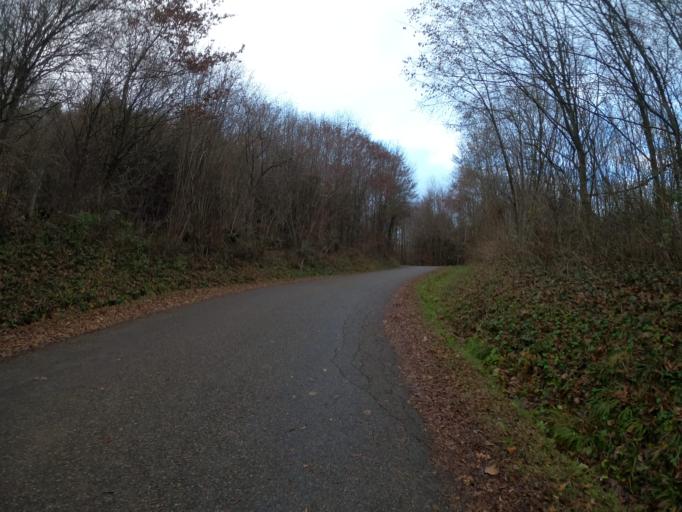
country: DE
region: Baden-Wuerttemberg
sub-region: Regierungsbezirk Stuttgart
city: Waschenbeuren
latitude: 48.7625
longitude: 9.7078
